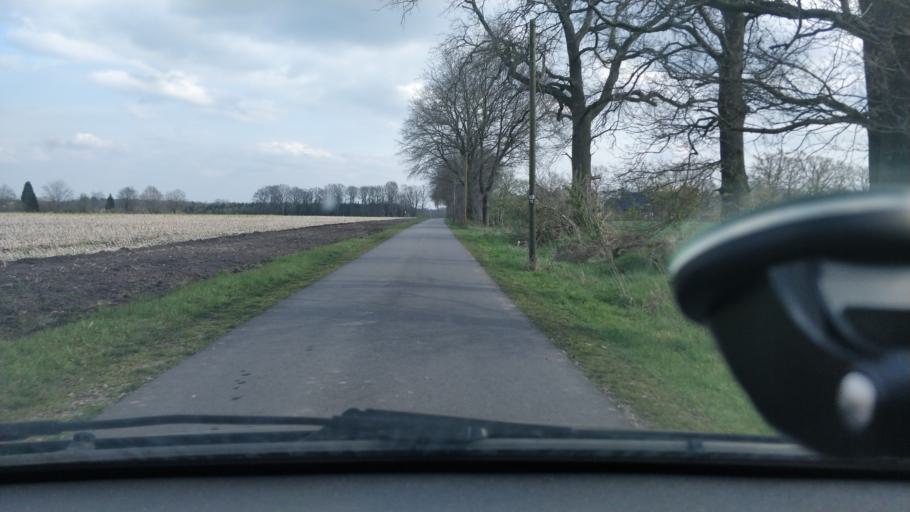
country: DE
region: North Rhine-Westphalia
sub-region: Regierungsbezirk Dusseldorf
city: Bocholt
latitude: 51.8889
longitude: 6.6316
